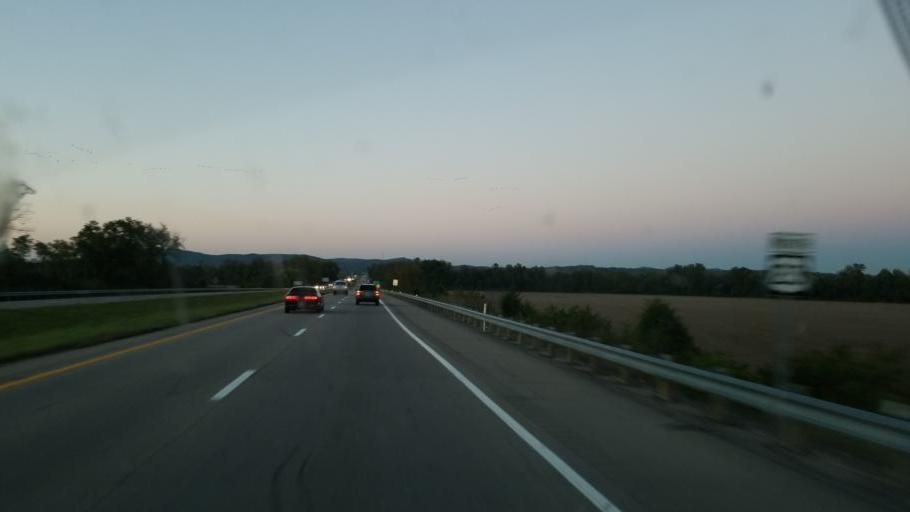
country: US
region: Ohio
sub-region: Ross County
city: Chillicothe
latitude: 39.2937
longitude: -82.9447
